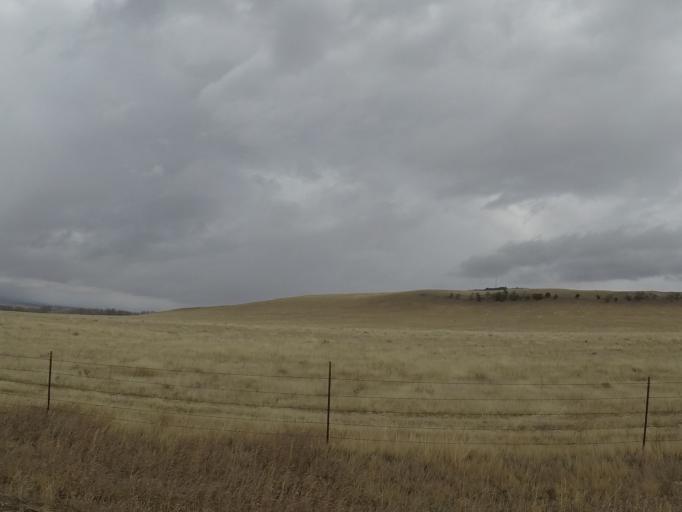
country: US
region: Montana
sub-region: Meagher County
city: White Sulphur Springs
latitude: 46.4258
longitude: -110.4173
